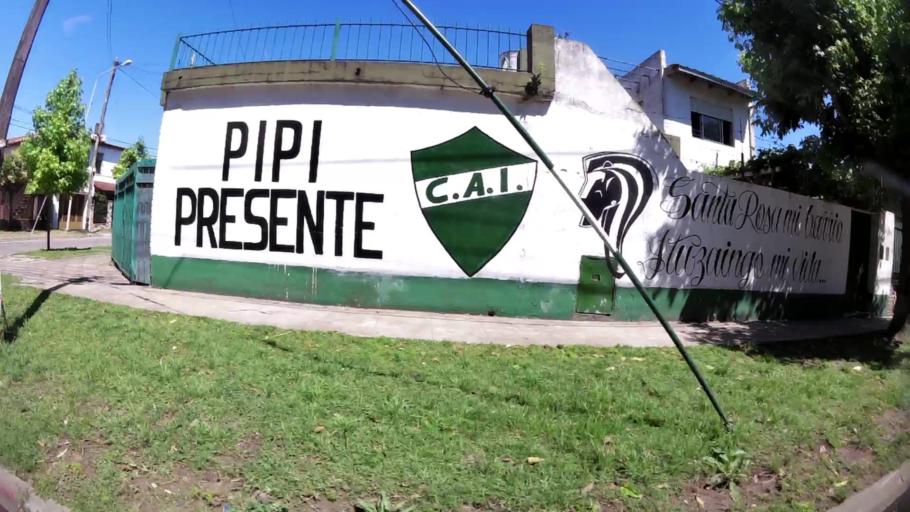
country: AR
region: Buenos Aires
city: Ituzaingo
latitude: -34.6709
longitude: -58.6611
